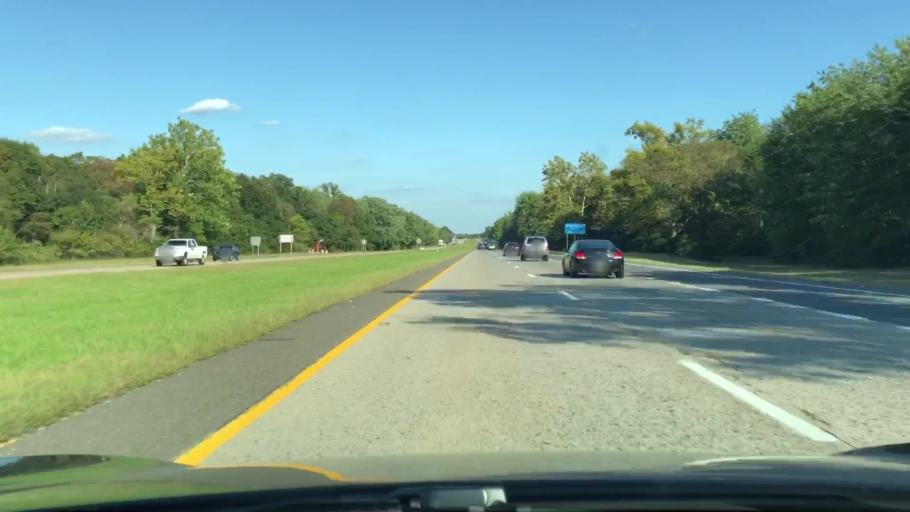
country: US
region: Pennsylvania
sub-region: Delaware County
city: Chester
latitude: 39.8029
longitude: -75.3391
